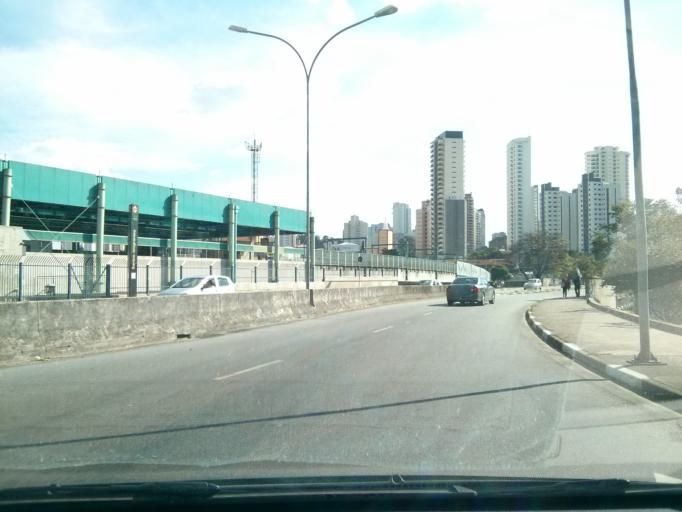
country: BR
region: Sao Paulo
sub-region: Sao Paulo
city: Sao Paulo
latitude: -23.5955
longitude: -46.6206
